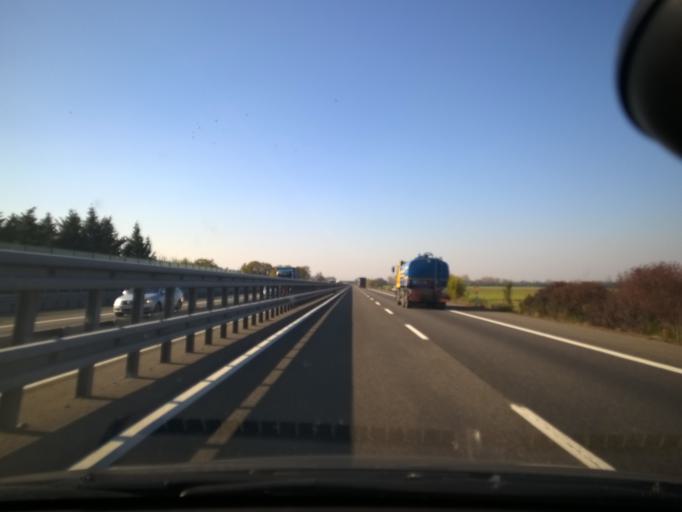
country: IT
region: Emilia-Romagna
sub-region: Provincia di Piacenza
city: San Nicolo
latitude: 45.0637
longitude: 9.6012
